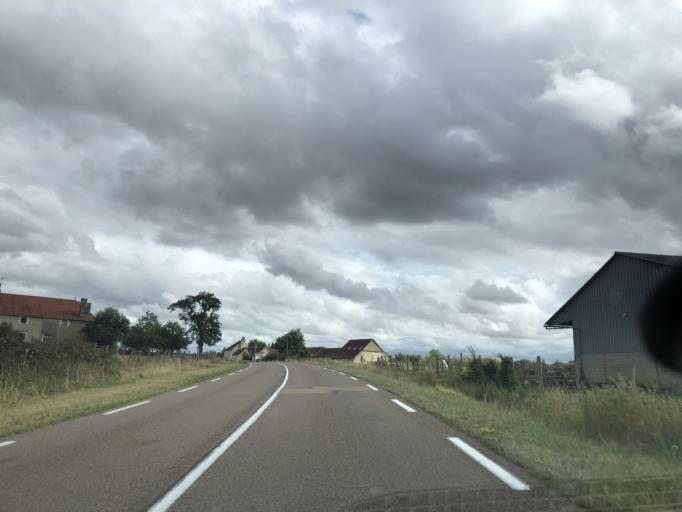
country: FR
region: Bourgogne
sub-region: Departement de l'Yonne
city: Charbuy
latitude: 47.8058
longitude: 3.4942
